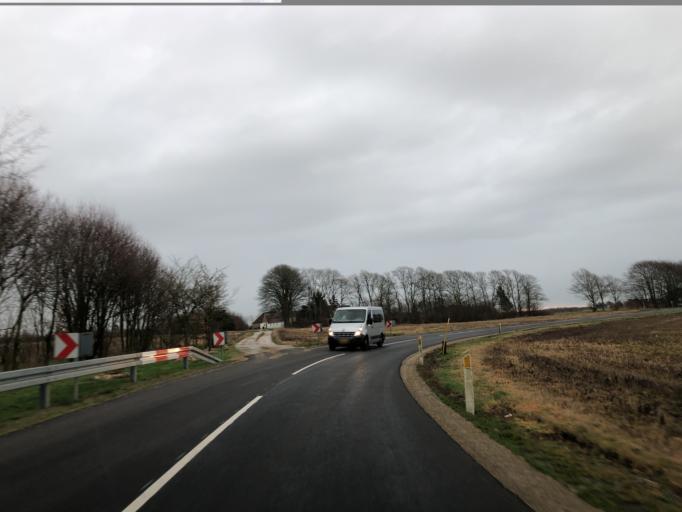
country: DK
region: Central Jutland
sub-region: Holstebro Kommune
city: Vinderup
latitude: 56.3790
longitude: 8.8463
